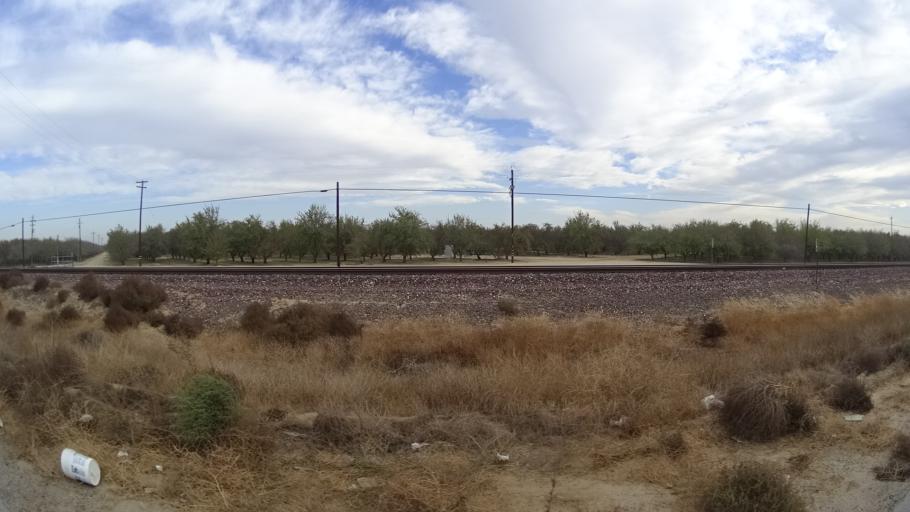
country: US
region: California
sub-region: Kern County
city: Rosedale
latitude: 35.4270
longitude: -119.1809
